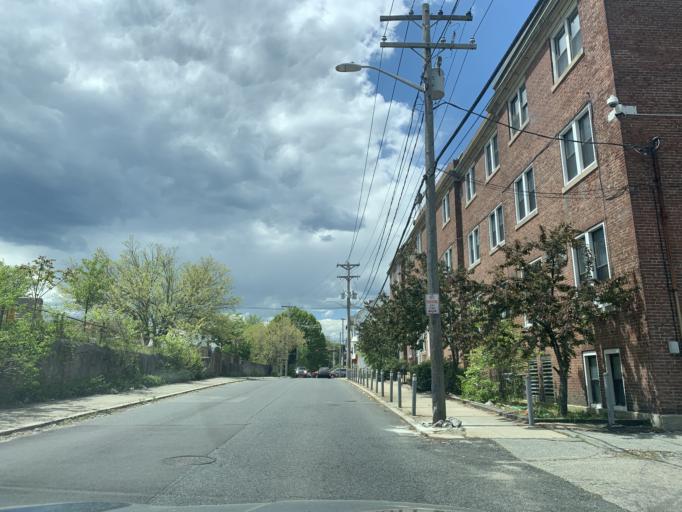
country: US
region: Rhode Island
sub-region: Providence County
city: Providence
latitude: 41.8399
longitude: -71.4248
